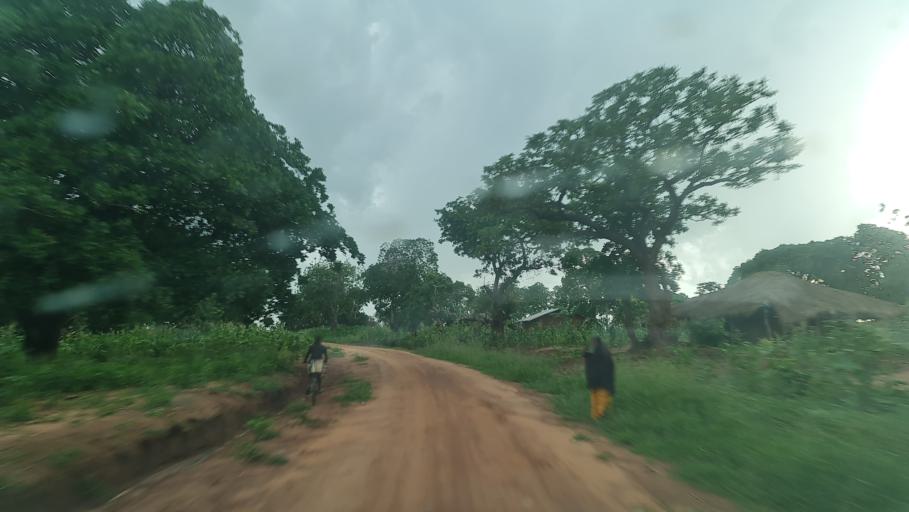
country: MZ
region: Nampula
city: Nacala
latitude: -14.0020
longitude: 40.3576
